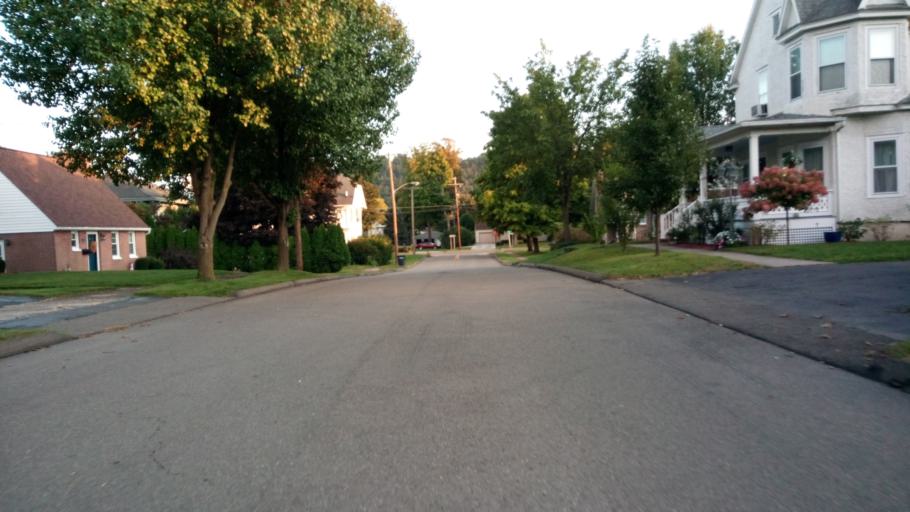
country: US
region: New York
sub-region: Chemung County
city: West Elmira
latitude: 42.0808
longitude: -76.8349
